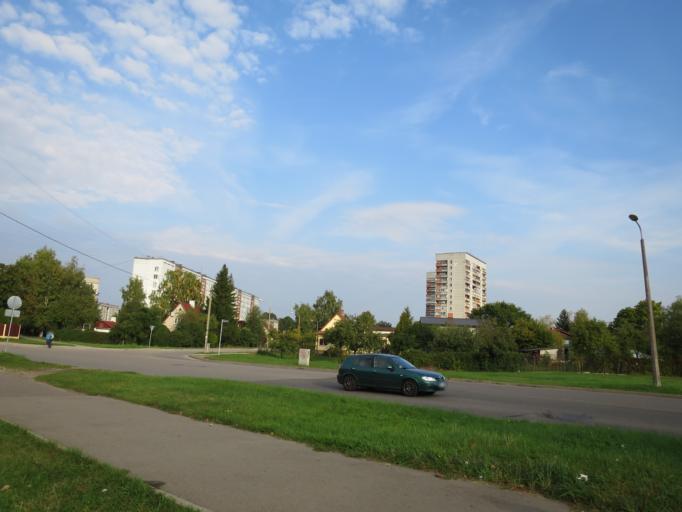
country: LV
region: Stopini
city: Ulbroka
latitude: 56.9688
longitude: 24.2353
